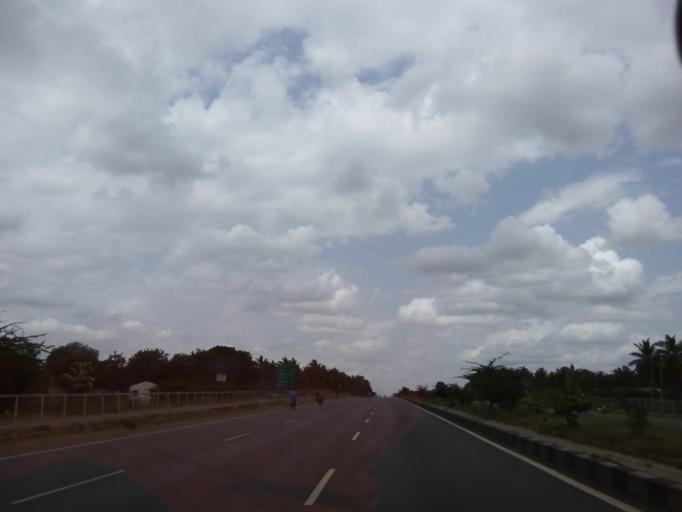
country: IN
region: Karnataka
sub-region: Chitradurga
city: Hiriyur
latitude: 13.9233
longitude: 76.6409
